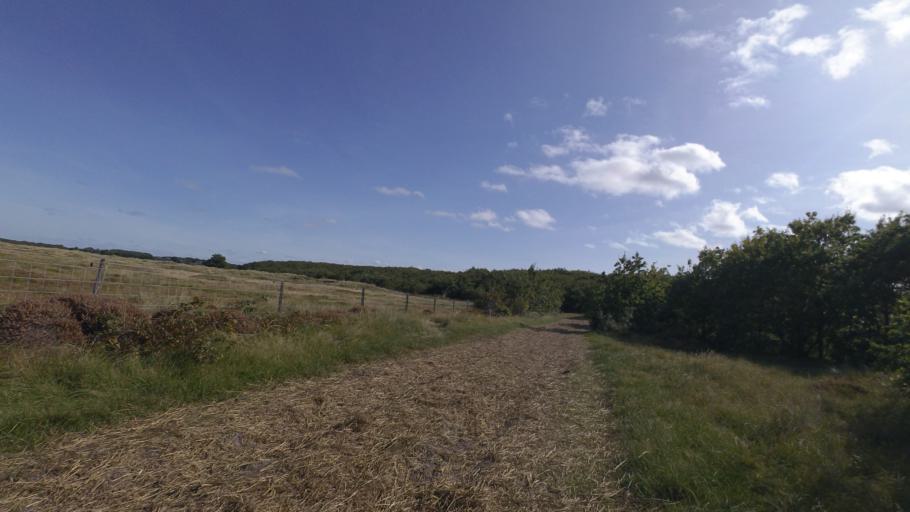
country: NL
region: Friesland
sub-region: Gemeente Ameland
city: Hollum
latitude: 53.4511
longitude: 5.6967
